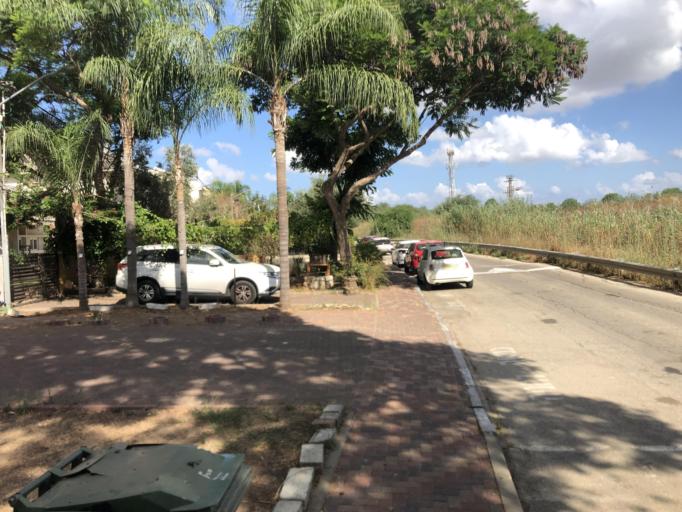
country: IL
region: Central District
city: Yehud
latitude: 32.0407
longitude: 34.8957
